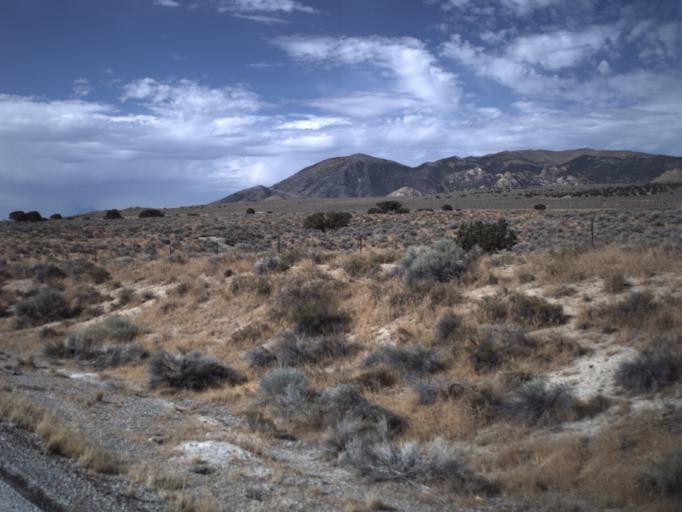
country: US
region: Utah
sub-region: Tooele County
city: Wendover
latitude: 41.5260
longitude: -113.5955
